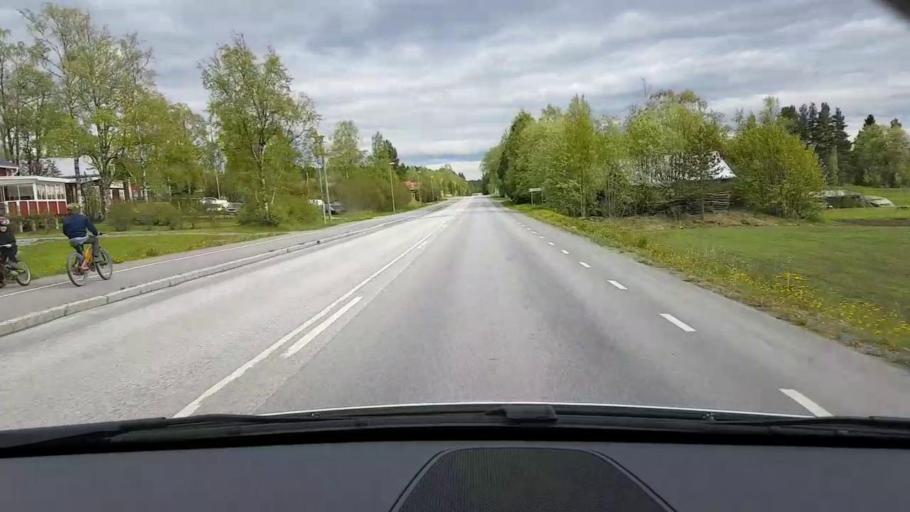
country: SE
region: Jaemtland
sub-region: OEstersunds Kommun
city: Brunflo
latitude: 63.1148
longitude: 14.7884
